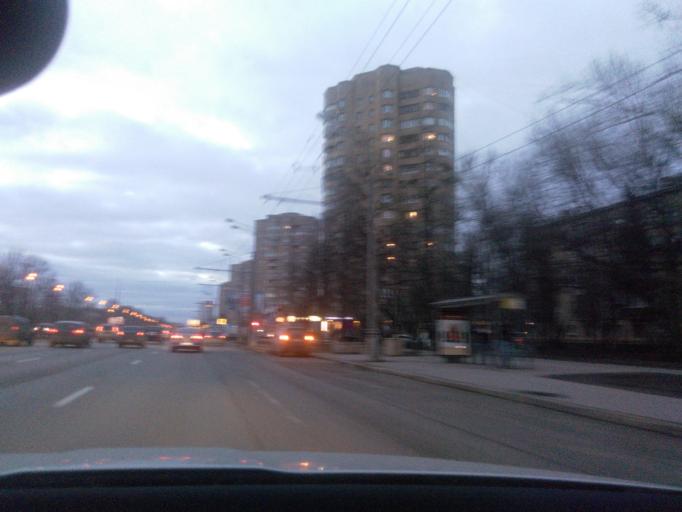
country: RU
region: Moskovskaya
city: Levoberezhnyy
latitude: 55.8441
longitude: 37.4782
